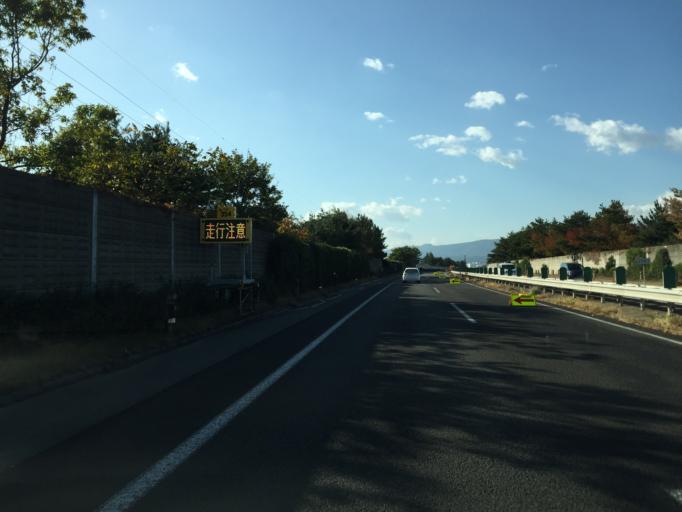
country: JP
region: Fukushima
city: Fukushima-shi
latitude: 37.7698
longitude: 140.4127
